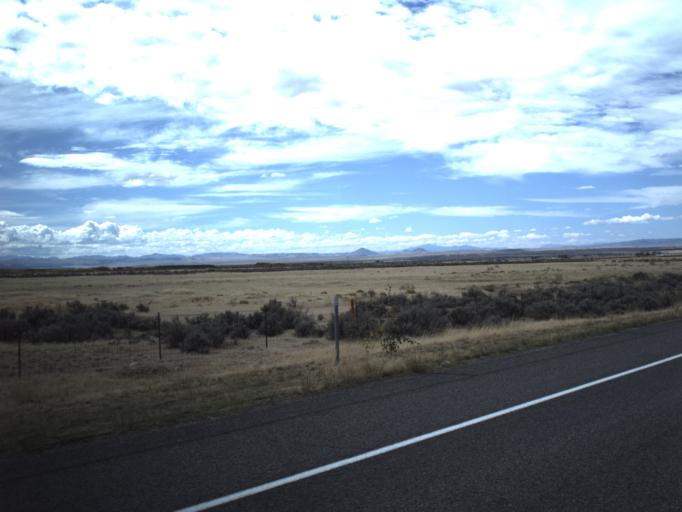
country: US
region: Utah
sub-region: Millard County
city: Fillmore
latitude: 38.9792
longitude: -112.3541
